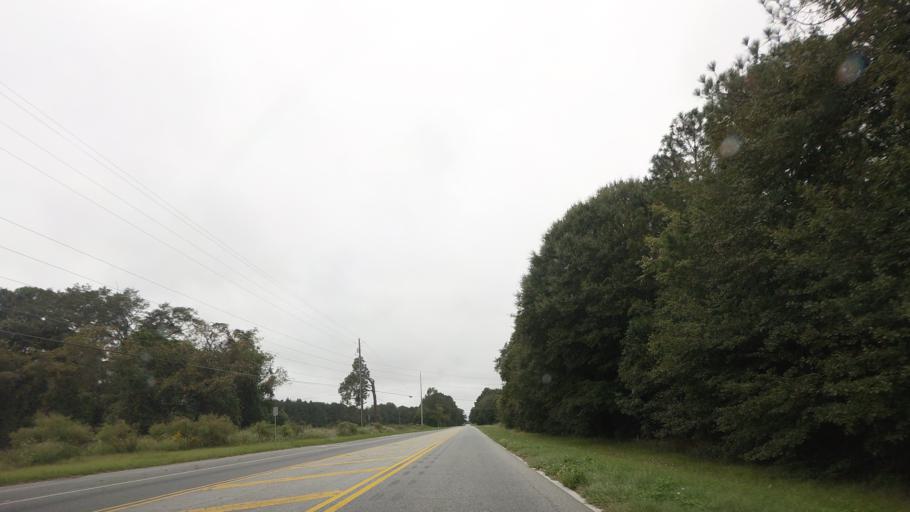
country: US
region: Georgia
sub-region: Lowndes County
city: Valdosta
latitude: 30.8155
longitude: -83.2503
